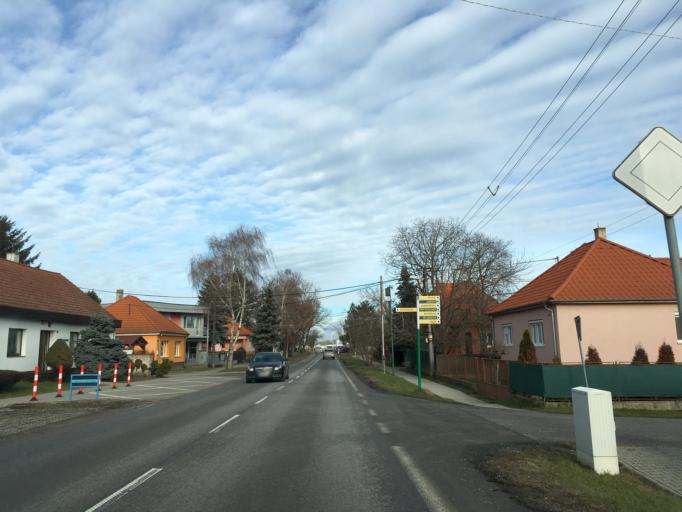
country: AT
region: Burgenland
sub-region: Politischer Bezirk Neusiedl am See
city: Deutsch Jahrndorf
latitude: 48.0669
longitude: 17.1150
